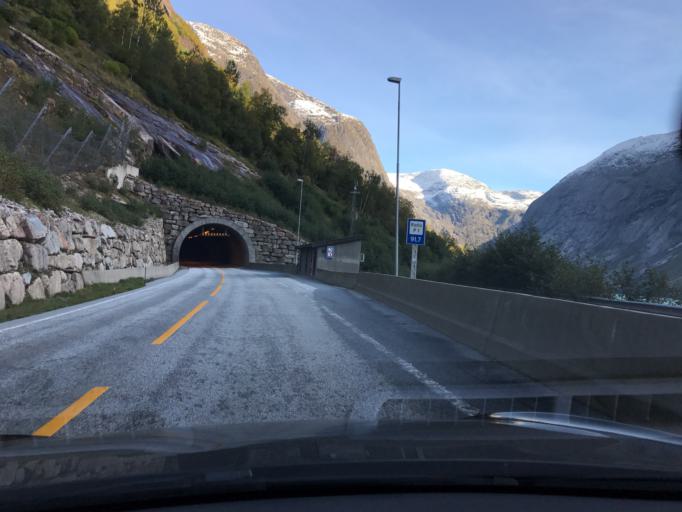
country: NO
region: Sogn og Fjordane
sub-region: Jolster
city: Skei
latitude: 61.5315
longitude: 6.5733
